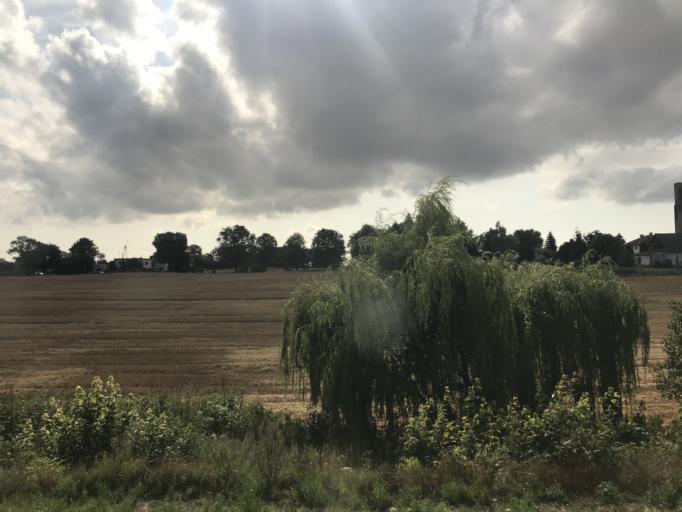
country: PL
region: Kujawsko-Pomorskie
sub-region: Powiat swiecki
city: Warlubie
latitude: 53.5940
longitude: 18.6267
